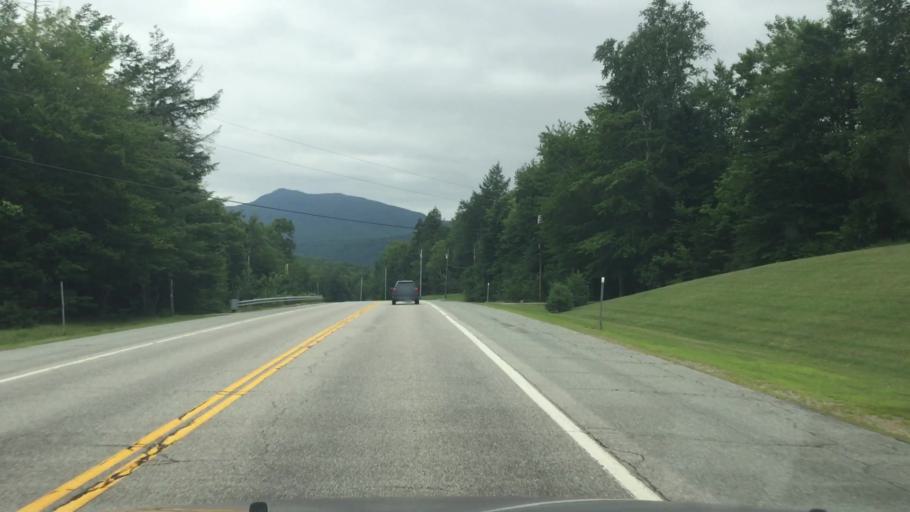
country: US
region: New Hampshire
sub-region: Carroll County
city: North Conway
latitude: 44.1110
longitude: -71.3534
